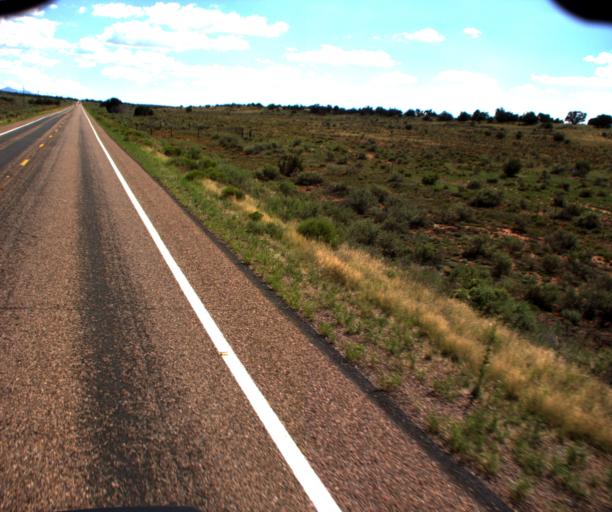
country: US
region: Arizona
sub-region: Coconino County
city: Williams
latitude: 35.5755
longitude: -112.1538
